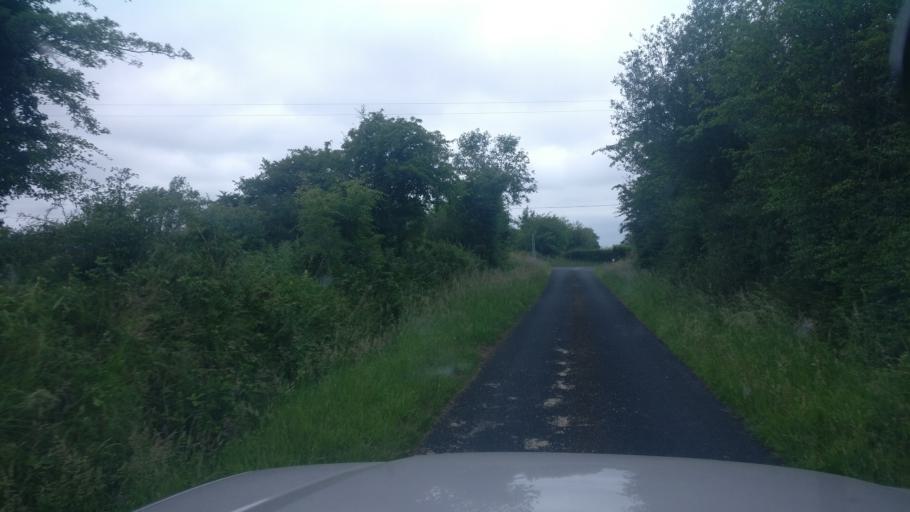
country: IE
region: Connaught
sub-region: County Galway
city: Ballinasloe
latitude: 53.3024
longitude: -8.3645
